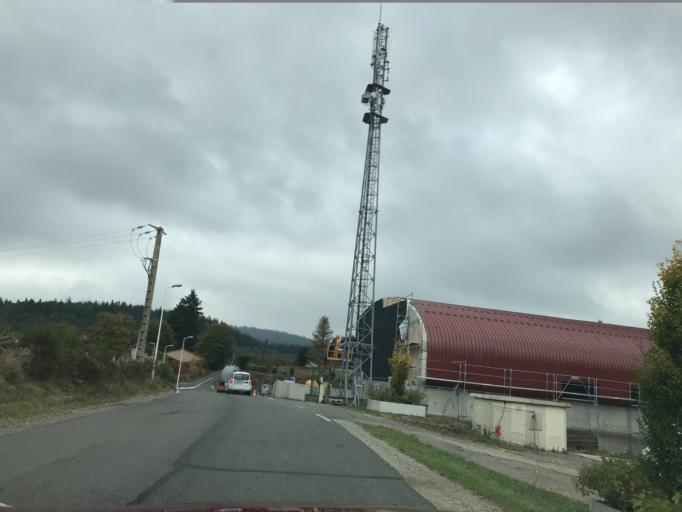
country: FR
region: Rhone-Alpes
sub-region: Departement de la Loire
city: Noiretable
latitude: 45.8200
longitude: 3.7594
